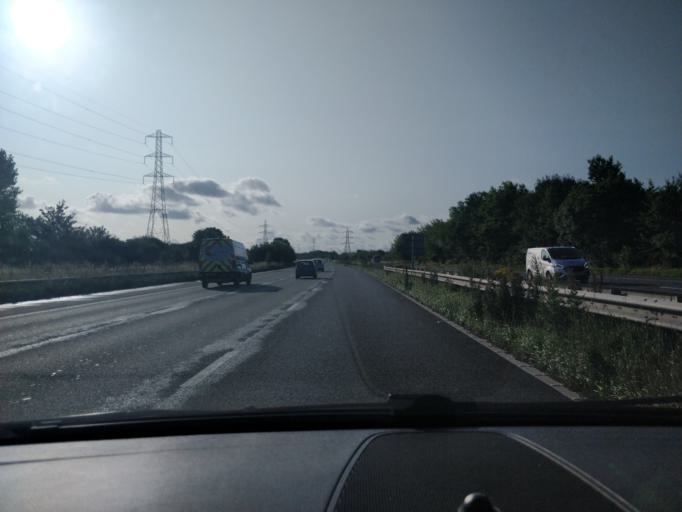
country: GB
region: England
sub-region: Sefton
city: Melling
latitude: 53.4869
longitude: -2.9352
